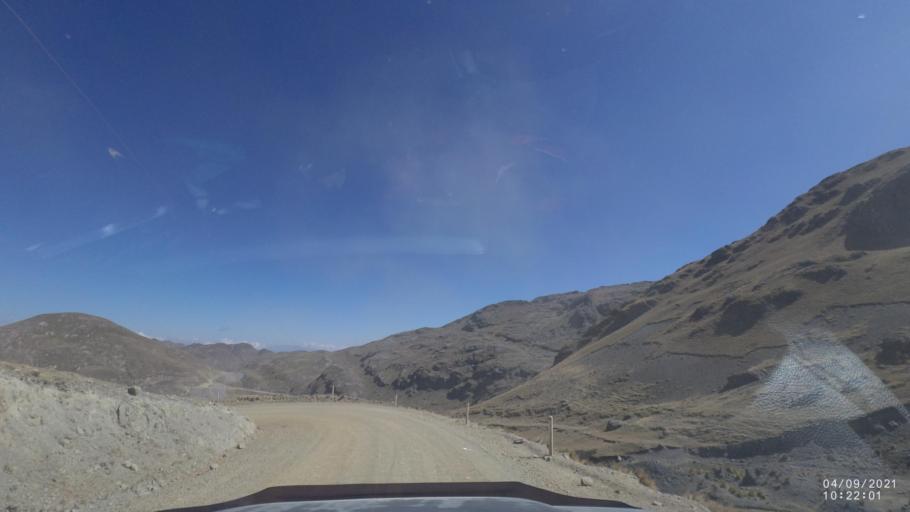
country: BO
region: Cochabamba
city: Sipe Sipe
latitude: -17.3088
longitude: -66.4341
